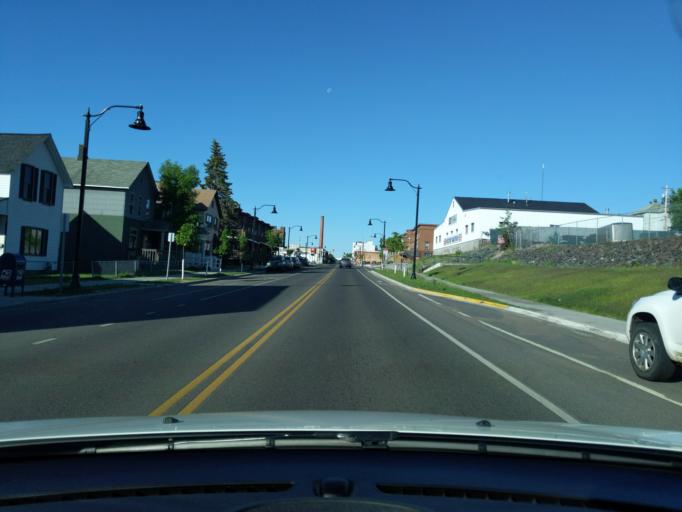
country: US
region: Minnesota
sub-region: Saint Louis County
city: Duluth
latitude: 46.7973
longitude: -92.0927
